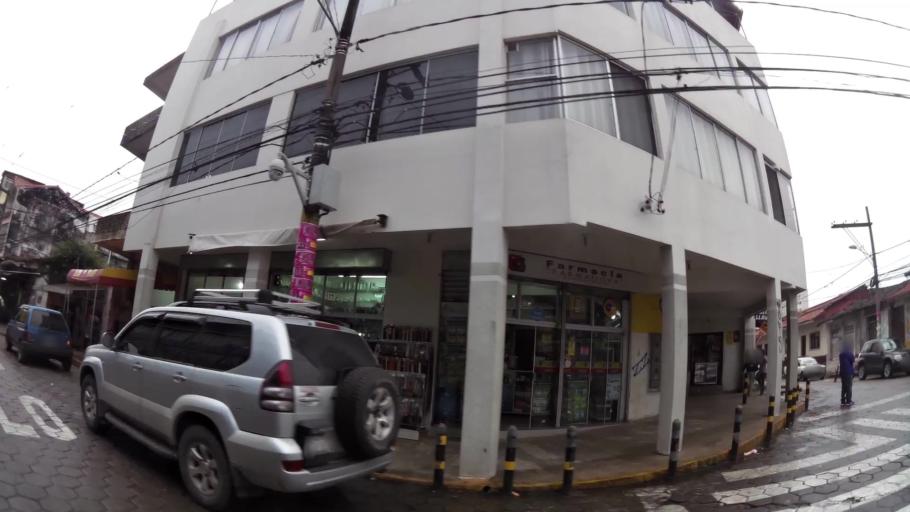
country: BO
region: Santa Cruz
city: Santa Cruz de la Sierra
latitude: -17.7875
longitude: -63.1854
